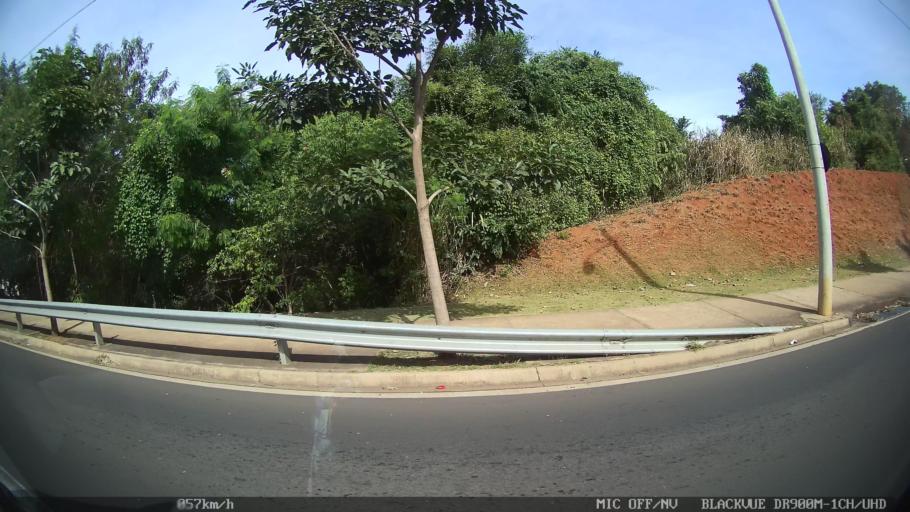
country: BR
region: Sao Paulo
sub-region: Piracicaba
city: Piracicaba
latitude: -22.7476
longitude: -47.6238
